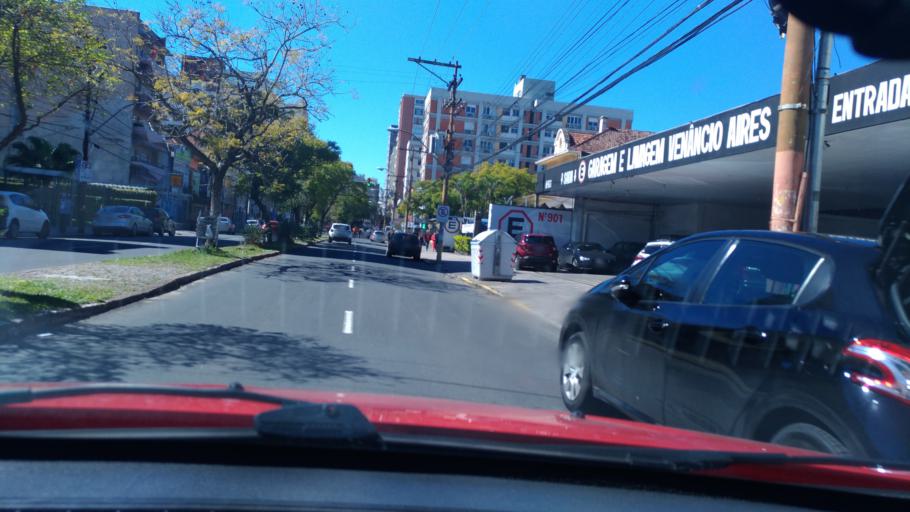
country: BR
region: Rio Grande do Sul
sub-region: Porto Alegre
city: Porto Alegre
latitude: -30.0386
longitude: -51.2119
